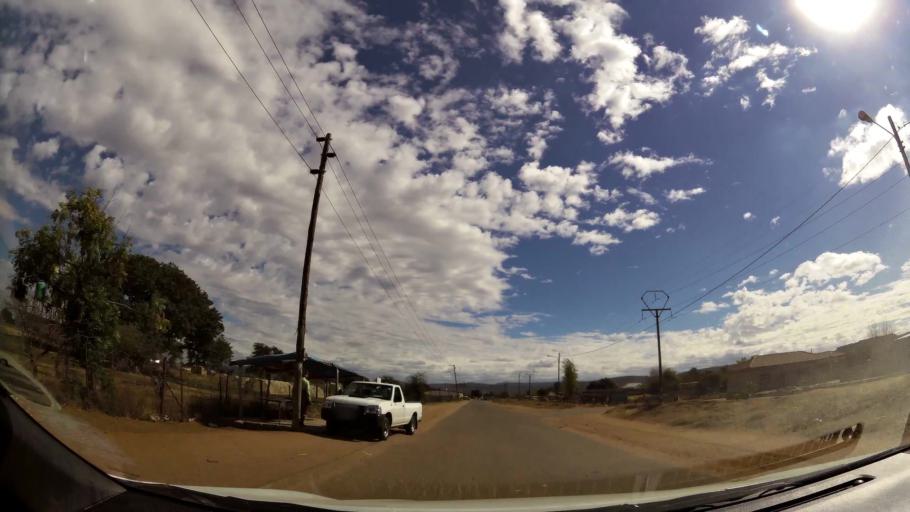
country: ZA
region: Limpopo
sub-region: Waterberg District Municipality
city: Bela-Bela
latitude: -24.8809
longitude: 28.3236
